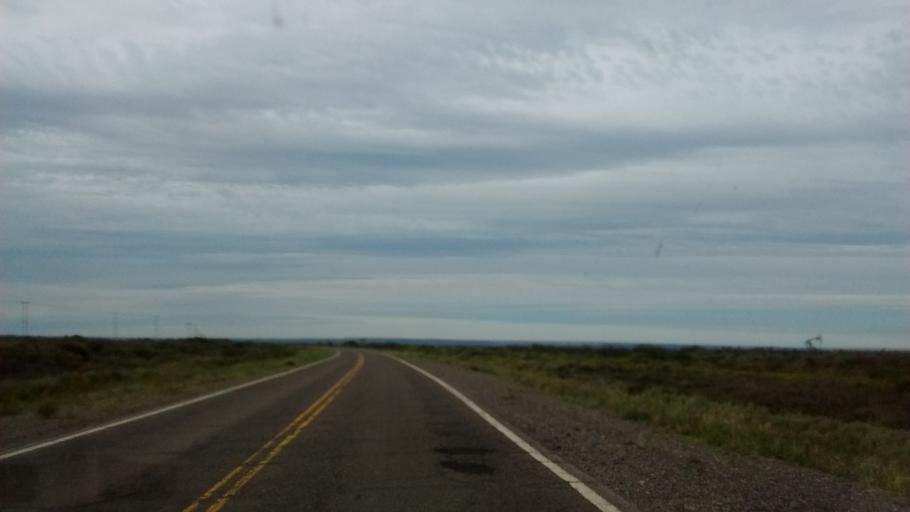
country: AR
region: Rio Negro
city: Catriel
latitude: -37.9794
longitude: -67.9073
